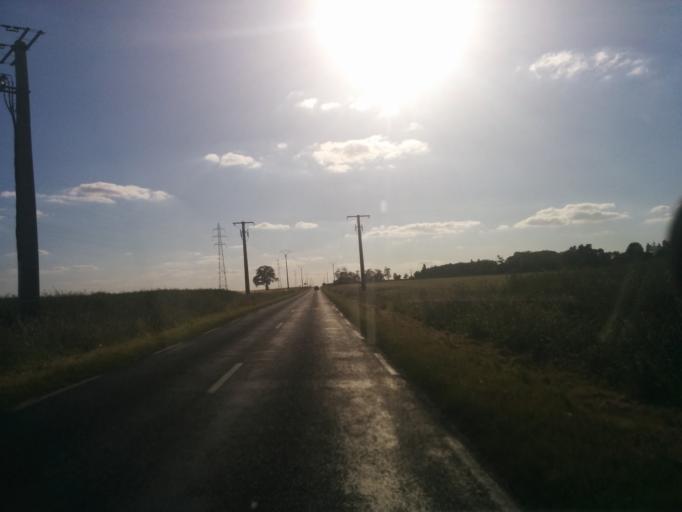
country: FR
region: Ile-de-France
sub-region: Departement des Yvelines
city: Limetz-Villez
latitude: 49.0946
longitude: 1.5643
